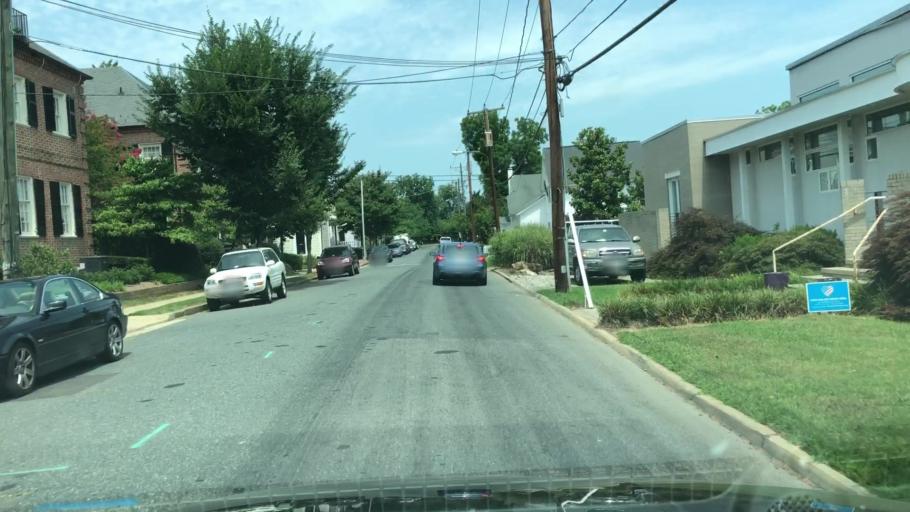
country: US
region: Virginia
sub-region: City of Fredericksburg
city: Fredericksburg
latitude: 38.3066
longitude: -77.4602
